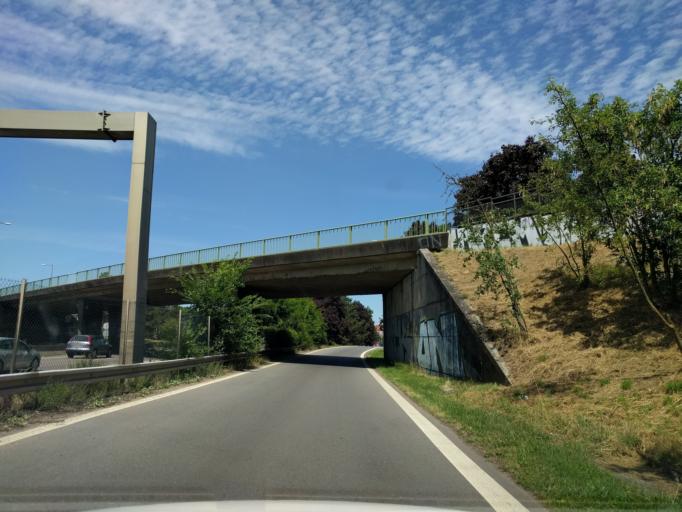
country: FR
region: Lorraine
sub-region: Departement de la Moselle
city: Le Ban Saint-Martin
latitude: 49.1275
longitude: 6.1623
